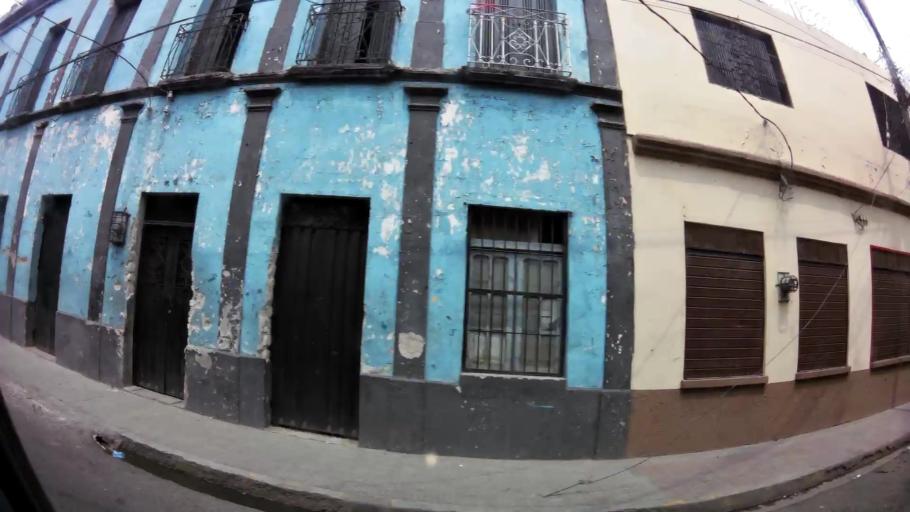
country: HN
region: Francisco Morazan
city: Tegucigalpa
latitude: 14.0980
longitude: -87.2063
